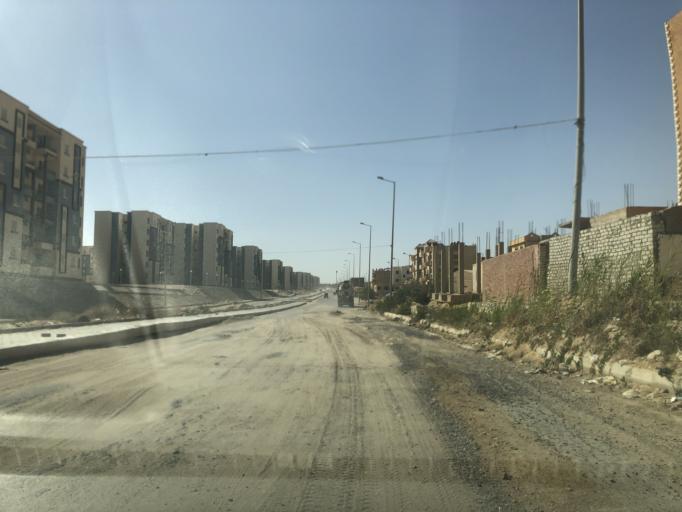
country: EG
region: Al Jizah
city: Madinat Sittah Uktubar
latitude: 29.9293
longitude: 30.9908
